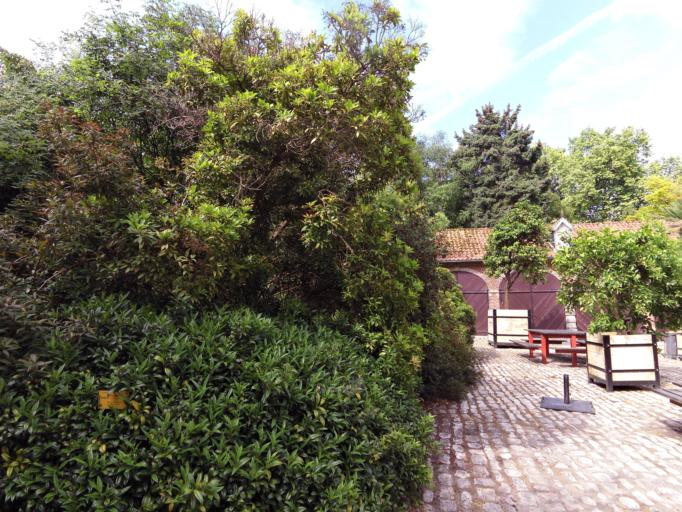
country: BE
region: Flanders
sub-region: Provincie Vlaams-Brabant
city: Meise
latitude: 50.9271
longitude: 4.3288
